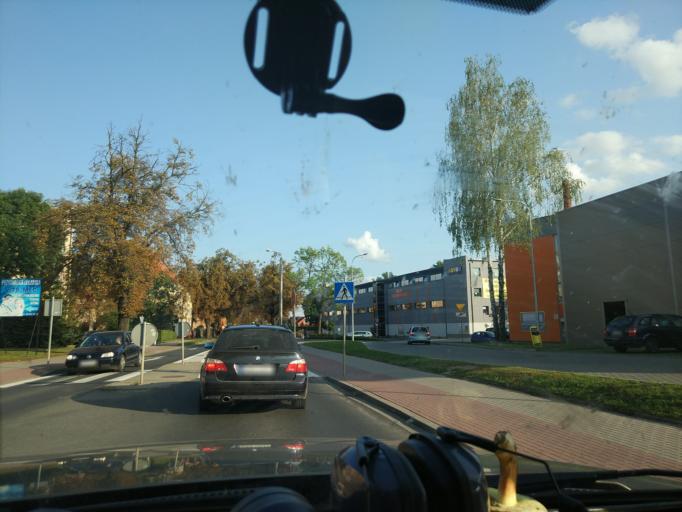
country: PL
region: Warmian-Masurian Voivodeship
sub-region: Powiat szczycienski
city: Szczytno
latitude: 53.5632
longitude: 20.9883
